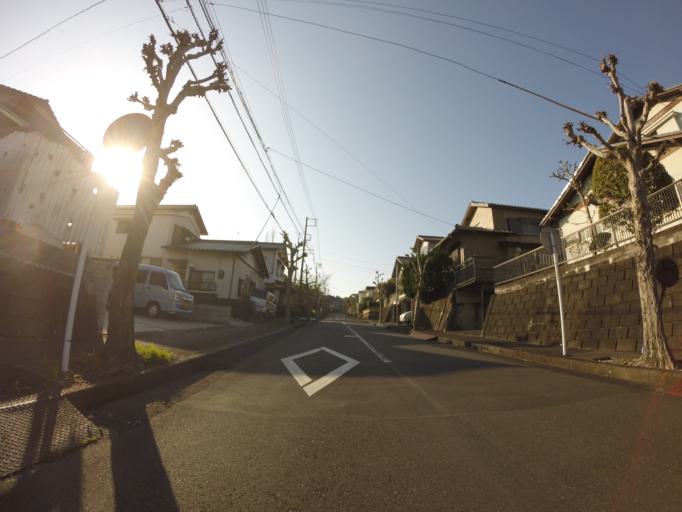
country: JP
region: Shizuoka
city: Shizuoka-shi
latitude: 34.9919
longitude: 138.4536
